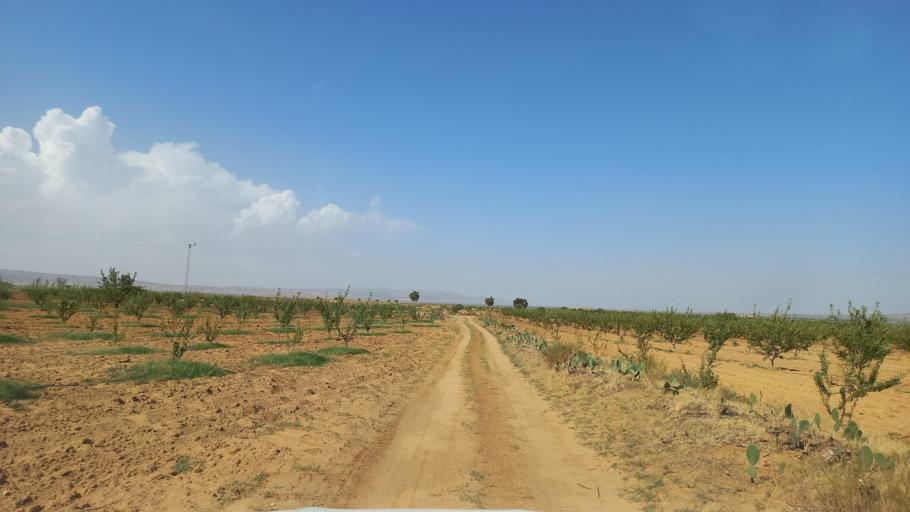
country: TN
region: Al Qasrayn
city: Kasserine
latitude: 35.2123
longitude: 9.0335
